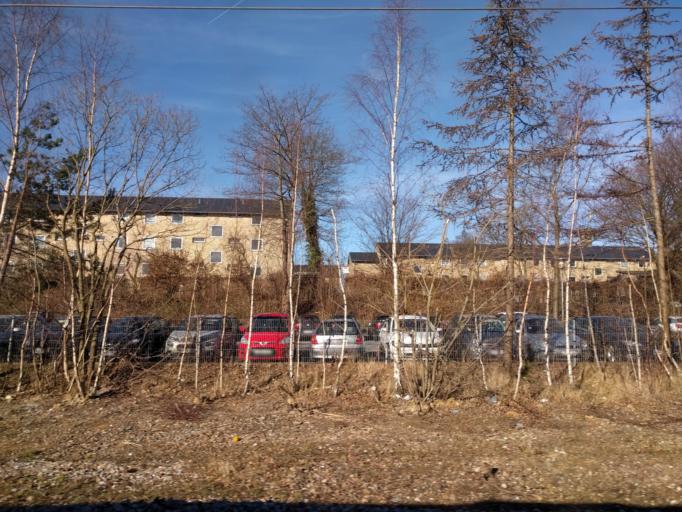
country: DK
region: Capital Region
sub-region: Helsingor Kommune
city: Espergaerde
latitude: 55.9941
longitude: 12.5476
